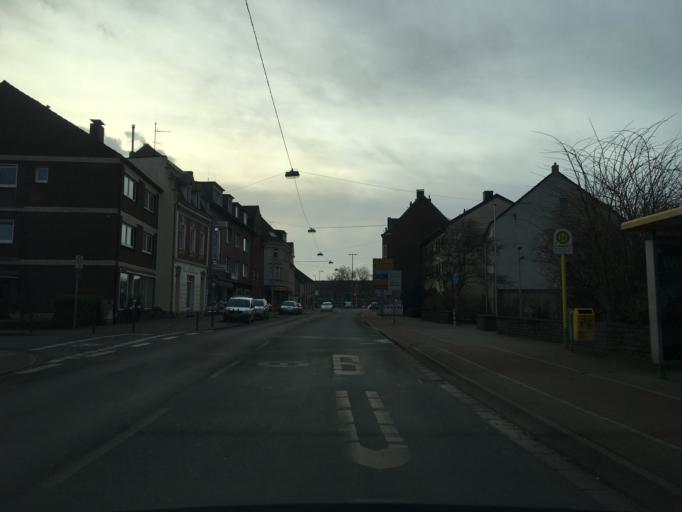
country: DE
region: North Rhine-Westphalia
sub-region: Regierungsbezirk Dusseldorf
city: Dinslaken
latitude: 51.5254
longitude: 6.7900
